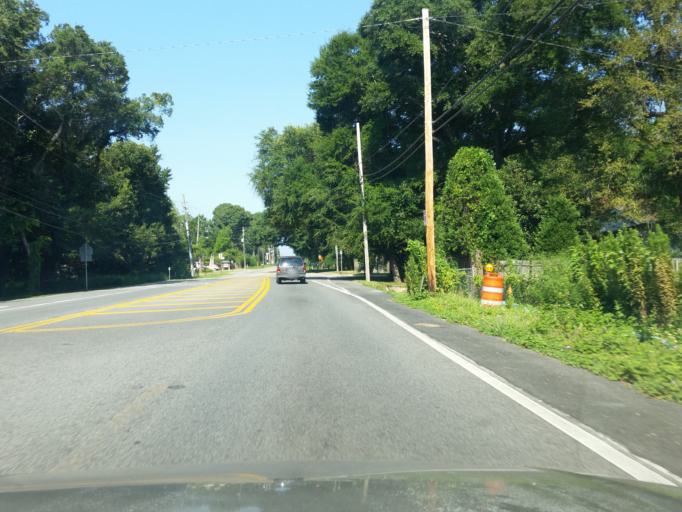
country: US
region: Florida
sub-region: Escambia County
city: Ferry Pass
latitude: 30.5100
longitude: -87.1978
